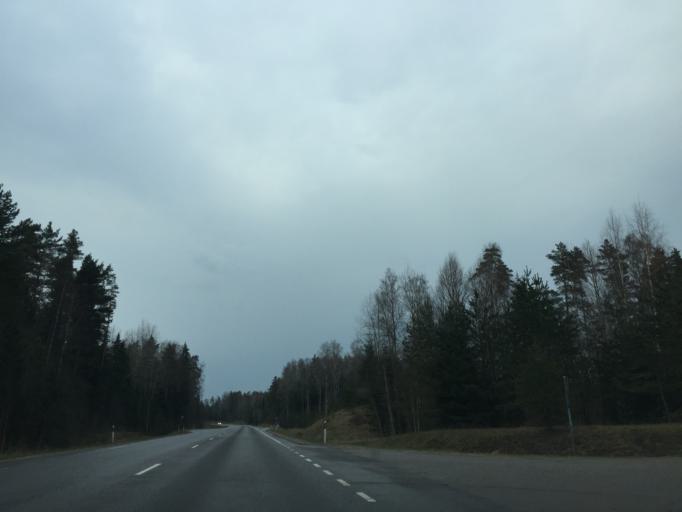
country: EE
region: Tartu
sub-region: UElenurme vald
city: Ulenurme
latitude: 58.1214
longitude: 26.7321
